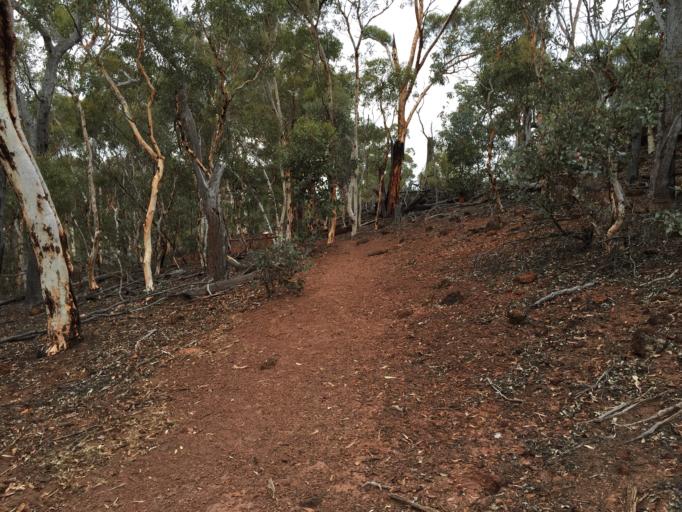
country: AU
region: Western Australia
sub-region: Narrogin
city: Narrogin
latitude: -32.7970
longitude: 116.9458
